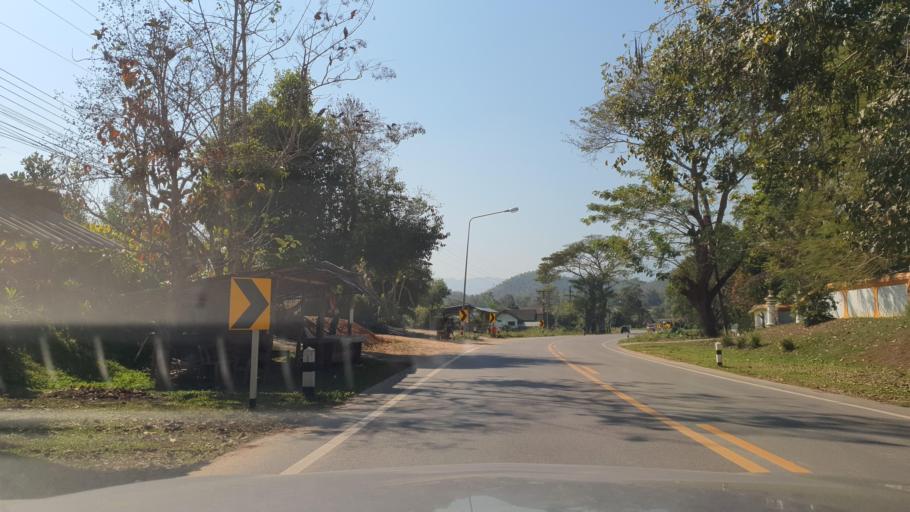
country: TH
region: Chiang Rai
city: Mae Lao
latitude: 19.8342
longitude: 99.6996
